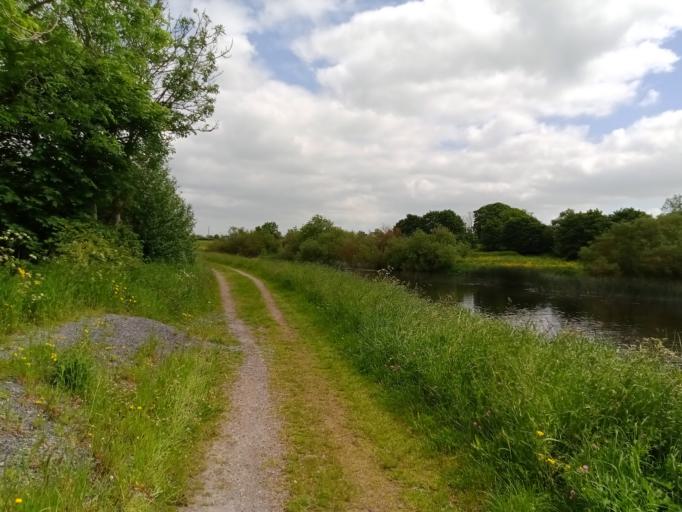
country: IE
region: Leinster
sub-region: County Carlow
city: Bagenalstown
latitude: 52.7462
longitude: -6.9704
